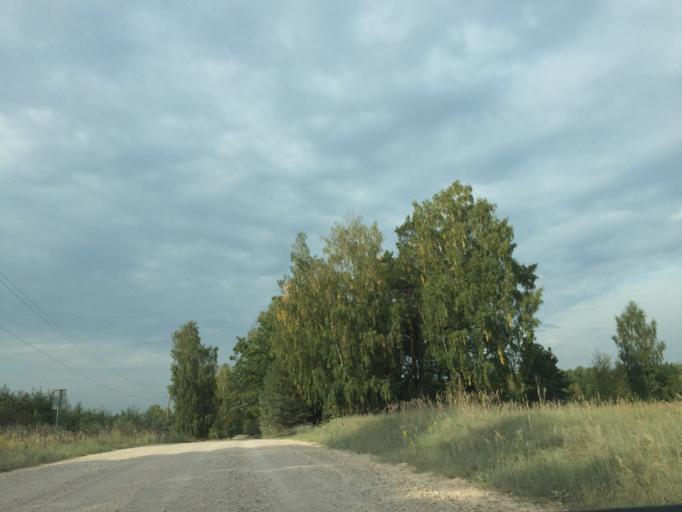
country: LV
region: Ikskile
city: Ikskile
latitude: 56.8143
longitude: 24.4480
